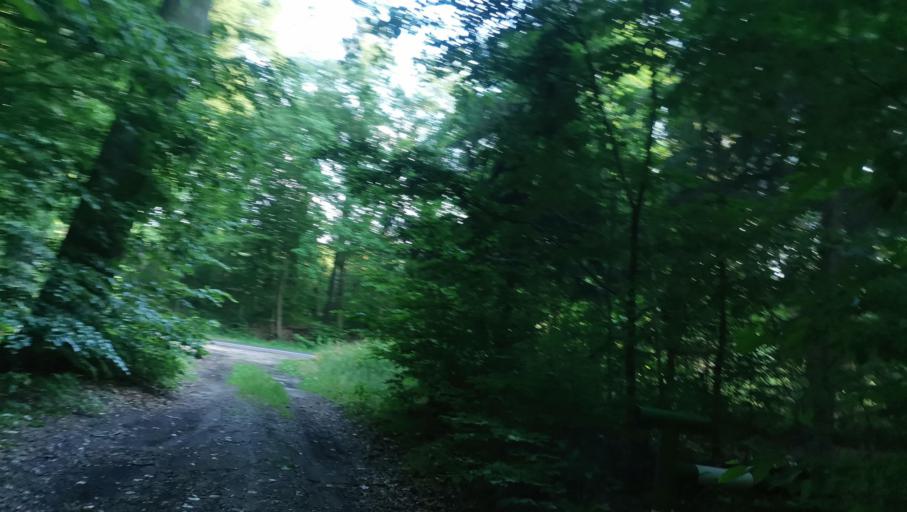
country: PL
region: Greater Poland Voivodeship
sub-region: Powiat jarocinski
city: Witaszyce
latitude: 51.9759
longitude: 17.5476
